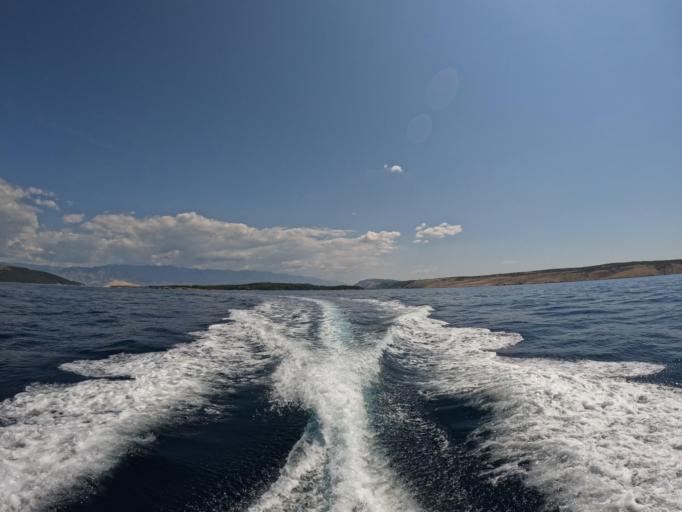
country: HR
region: Primorsko-Goranska
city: Lopar
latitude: 44.8556
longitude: 14.7020
